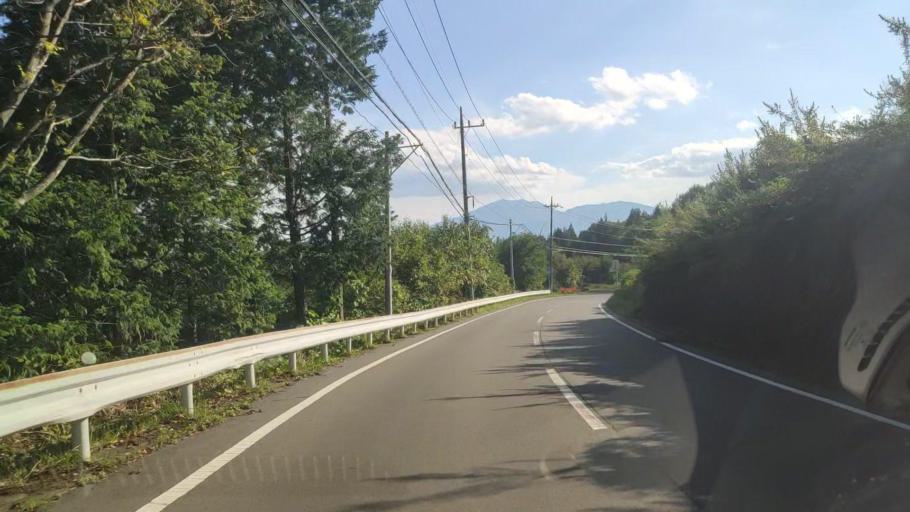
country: JP
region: Nagano
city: Suzaka
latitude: 36.5594
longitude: 138.5594
